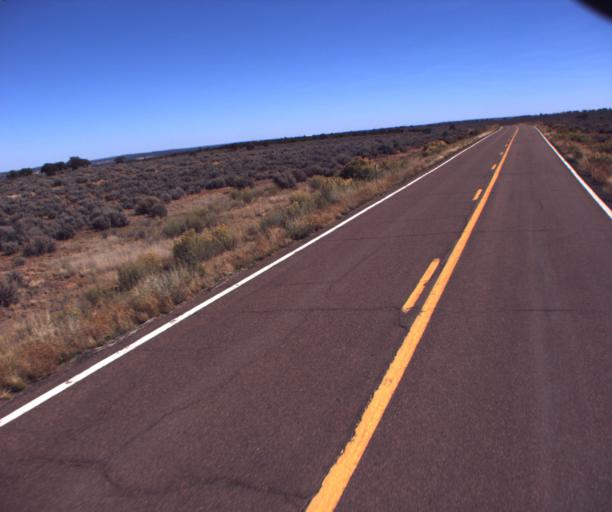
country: US
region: Arizona
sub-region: Apache County
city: Ganado
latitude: 35.7501
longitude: -109.9378
